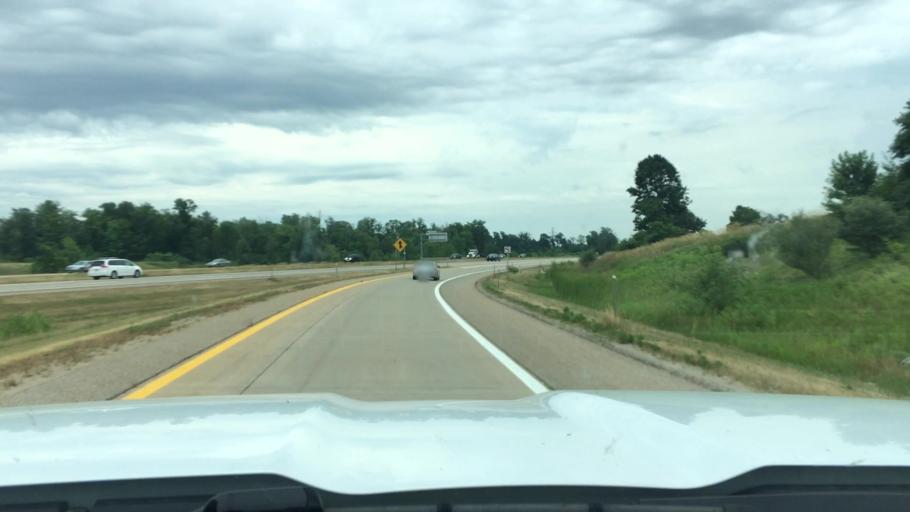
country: US
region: Michigan
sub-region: Kent County
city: Byron Center
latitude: 42.8523
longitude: -85.7179
